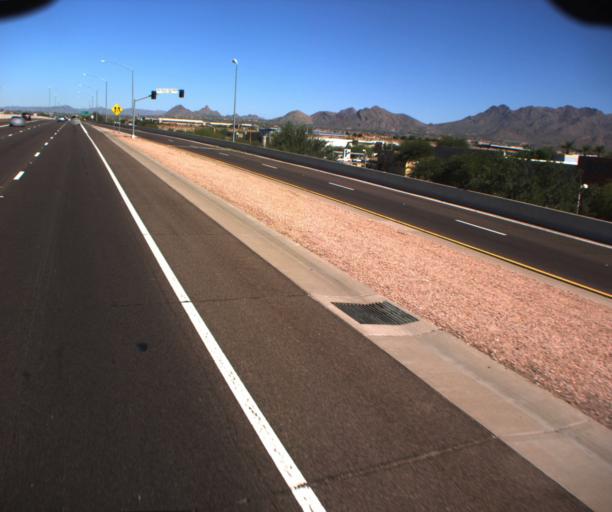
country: US
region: Arizona
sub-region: Maricopa County
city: Paradise Valley
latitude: 33.6280
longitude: -111.8902
